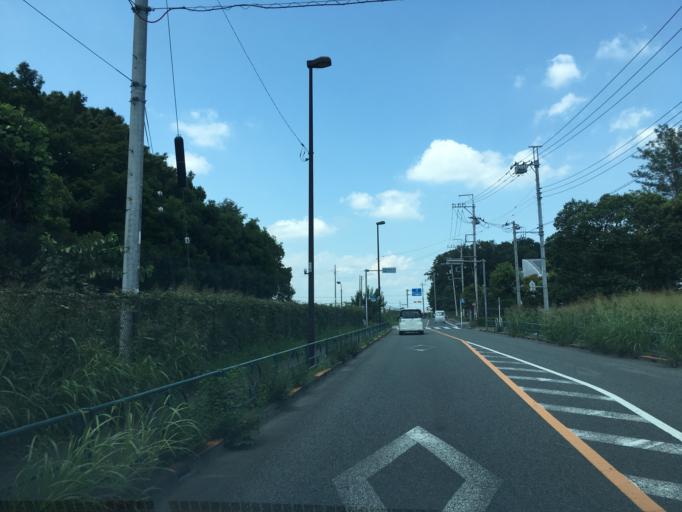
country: JP
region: Tokyo
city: Fussa
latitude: 35.7247
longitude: 139.3546
